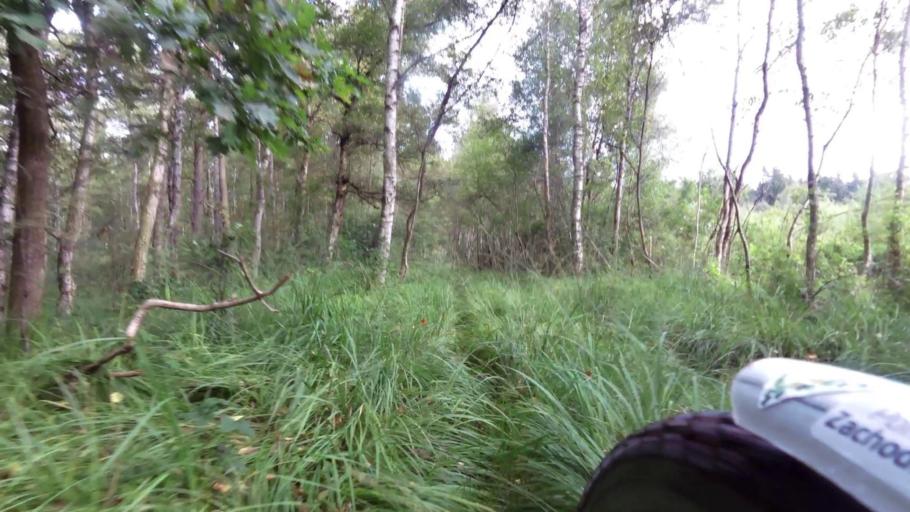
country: PL
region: West Pomeranian Voivodeship
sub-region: Powiat kolobrzeski
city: Grzybowo
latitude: 54.1609
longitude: 15.4580
